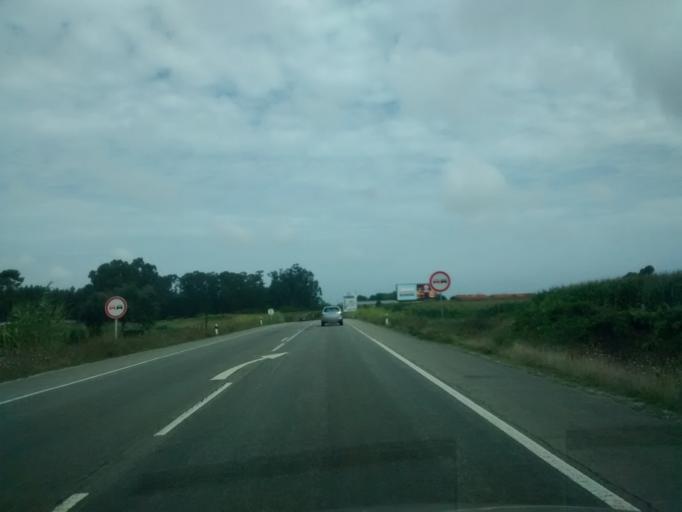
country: PT
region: Aveiro
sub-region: Aveiro
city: Aradas
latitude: 40.6084
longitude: -8.6240
